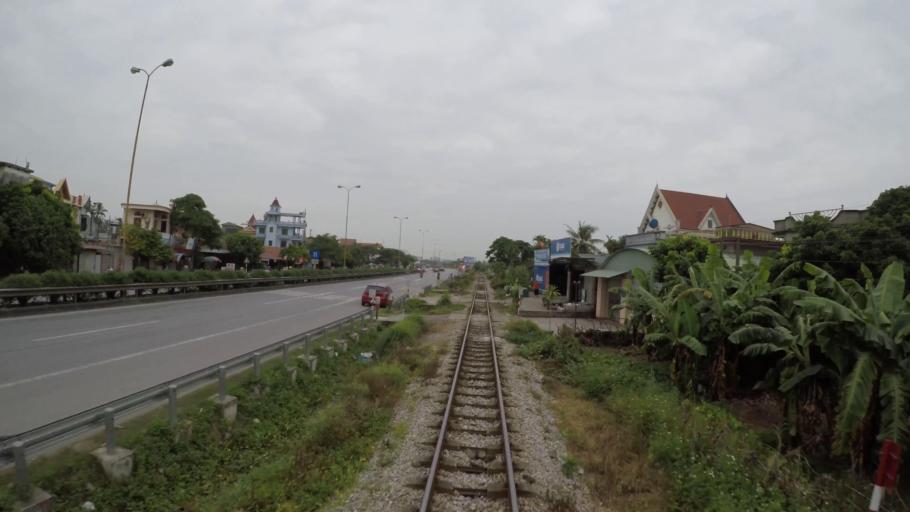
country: VN
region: Hai Duong
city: Phu Thai
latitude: 20.9537
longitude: 106.5300
